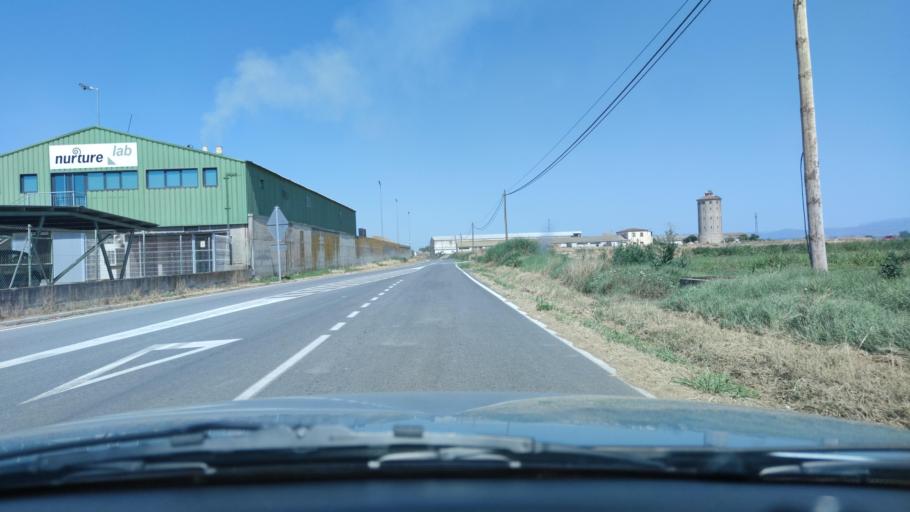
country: ES
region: Catalonia
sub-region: Provincia de Lleida
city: Ivars d'Urgell
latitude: 41.6851
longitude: 0.9799
